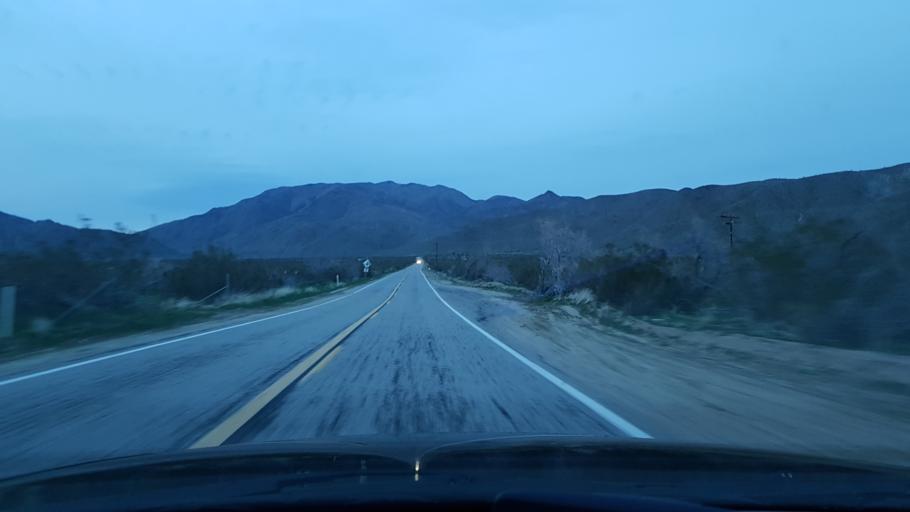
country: US
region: California
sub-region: San Diego County
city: Pine Valley
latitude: 32.9816
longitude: -116.4405
